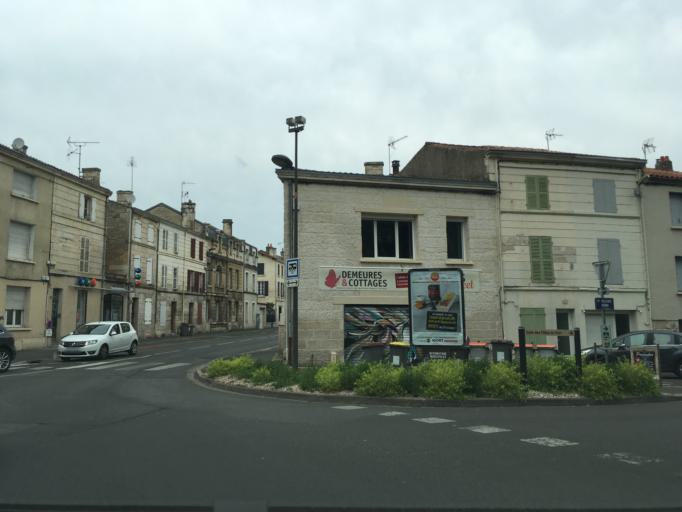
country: FR
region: Poitou-Charentes
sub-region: Departement des Deux-Sevres
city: Niort
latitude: 46.3258
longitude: -0.4683
